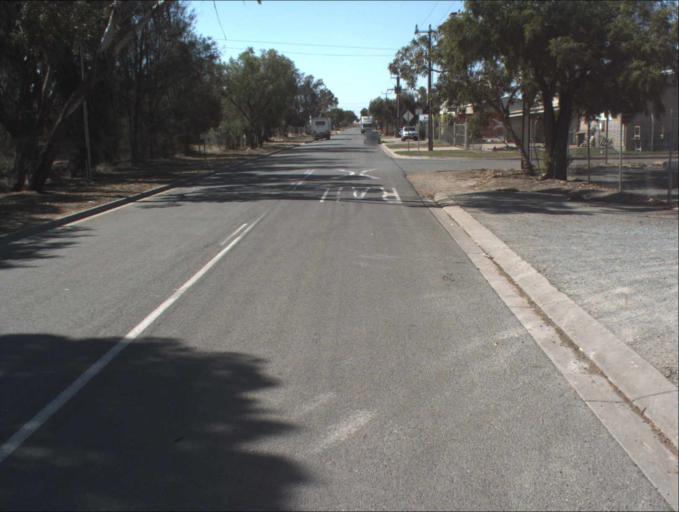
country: AU
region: South Australia
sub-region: Port Adelaide Enfield
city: Enfield
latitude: -34.8379
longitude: 138.5817
